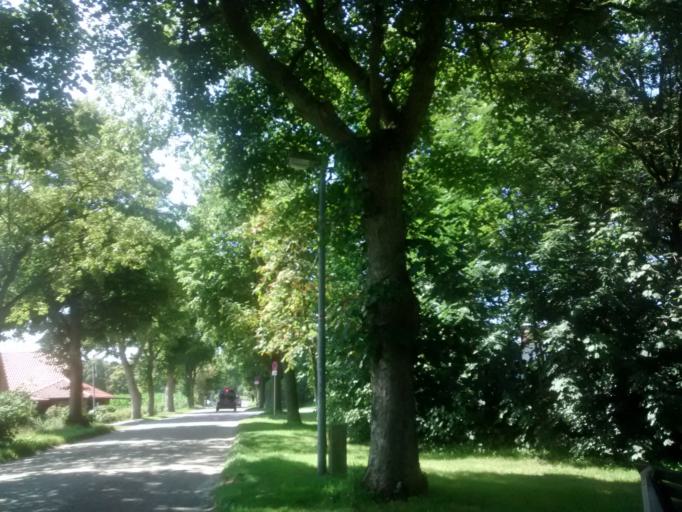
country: DE
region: Lower Saxony
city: Varel
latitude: 53.4446
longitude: 8.1199
